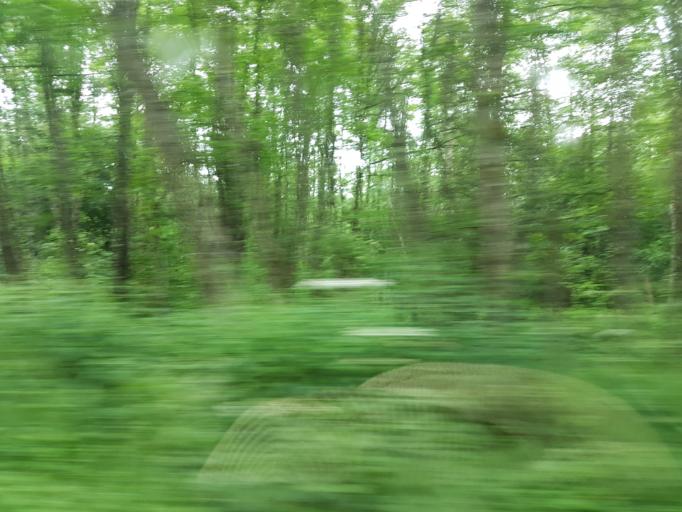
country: FR
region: Bourgogne
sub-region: Departement de la Nievre
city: Corbigny
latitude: 47.1776
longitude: 3.7481
